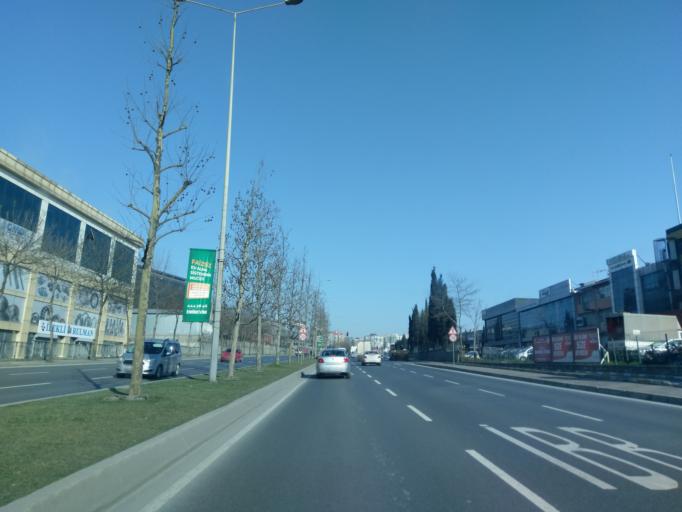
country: TR
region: Istanbul
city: Basaksehir
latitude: 41.0935
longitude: 28.7938
